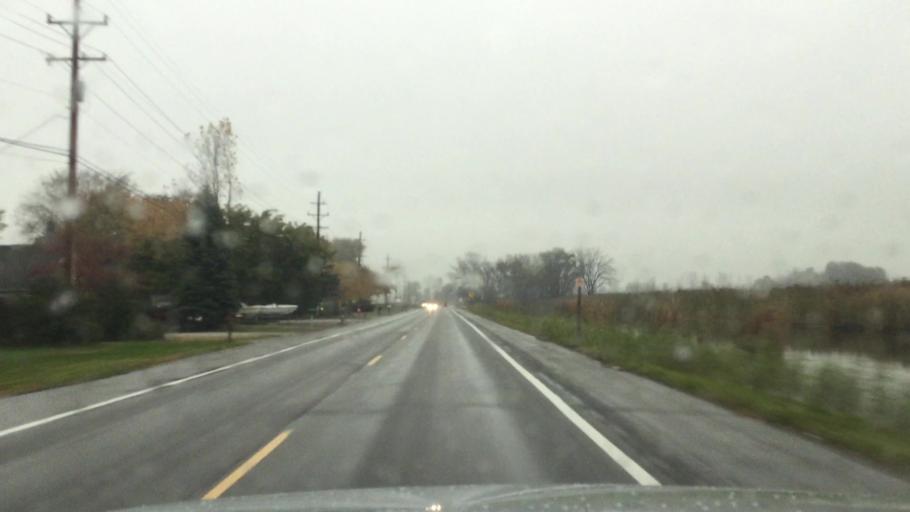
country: US
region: Michigan
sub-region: Saint Clair County
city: Pearl Beach
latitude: 42.6662
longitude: -82.6205
